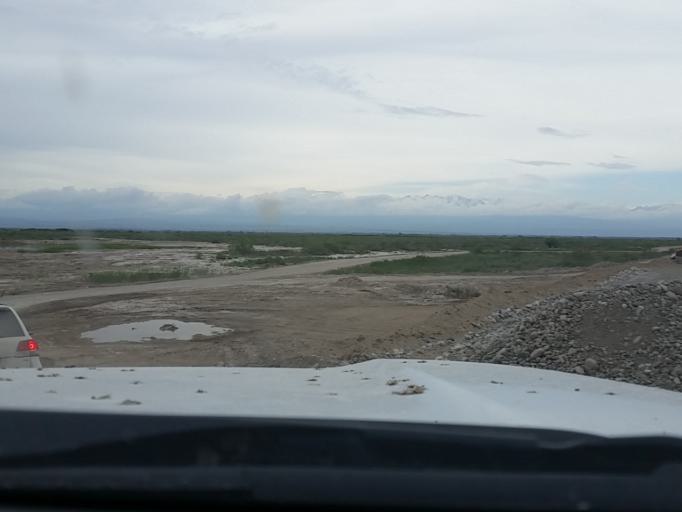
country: KZ
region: Almaty Oblysy
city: Zharkent
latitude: 44.0726
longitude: 80.0364
